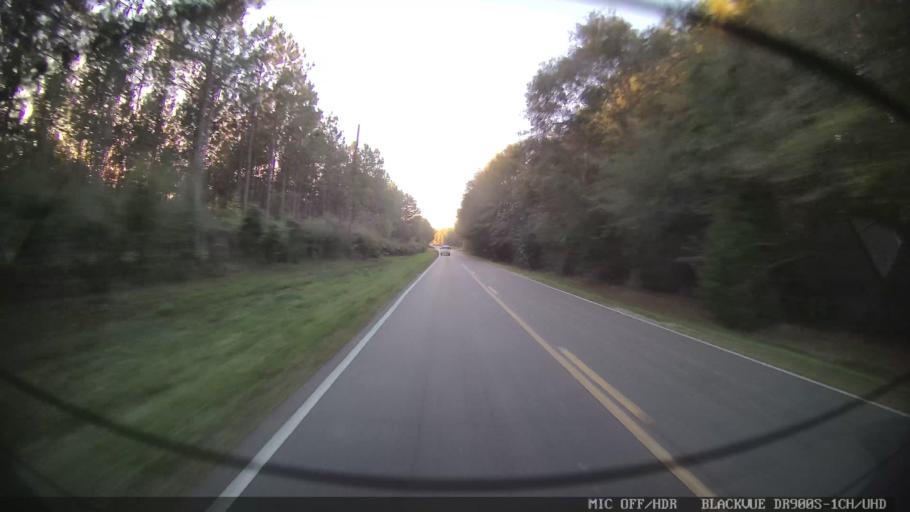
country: US
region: Mississippi
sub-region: Lamar County
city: Lumberton
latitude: 30.9988
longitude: -89.4065
